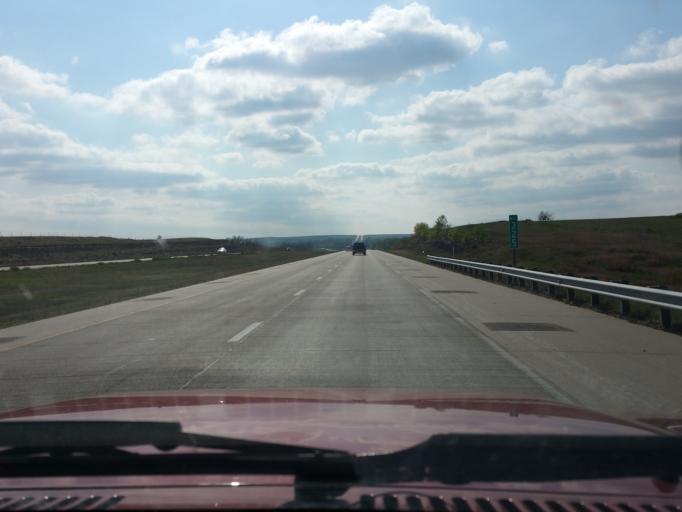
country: US
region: Kansas
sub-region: Wabaunsee County
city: Alma
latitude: 39.0657
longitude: -96.3347
